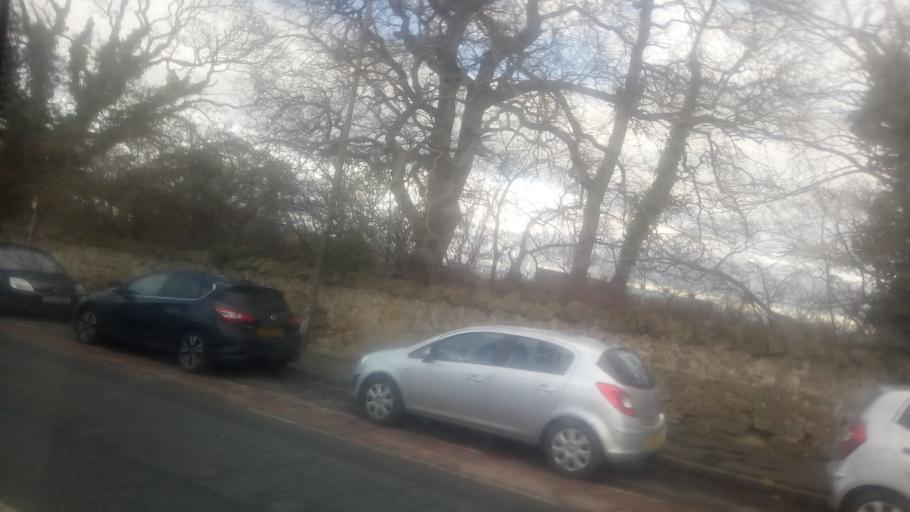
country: GB
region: Scotland
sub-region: Midlothian
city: Loanhead
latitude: 55.9165
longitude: -3.1312
